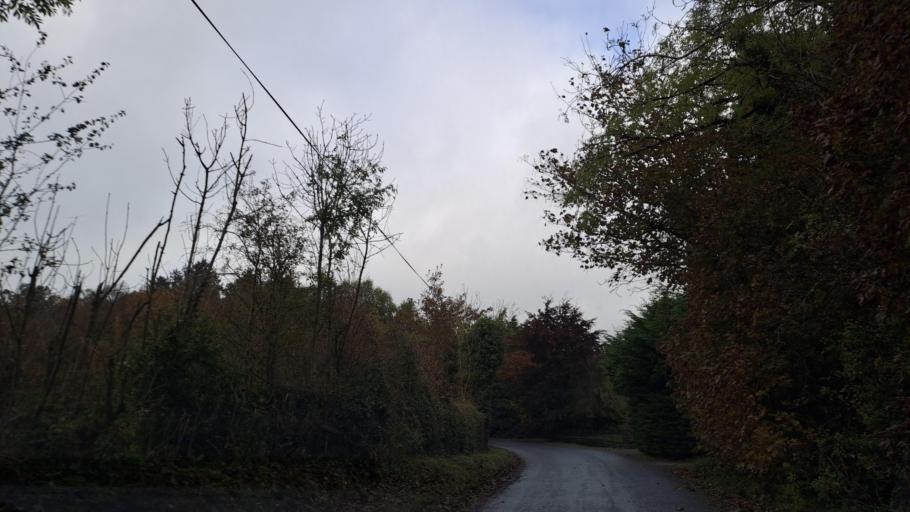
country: IE
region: Ulster
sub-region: An Cabhan
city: Bailieborough
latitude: 53.9907
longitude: -6.9901
